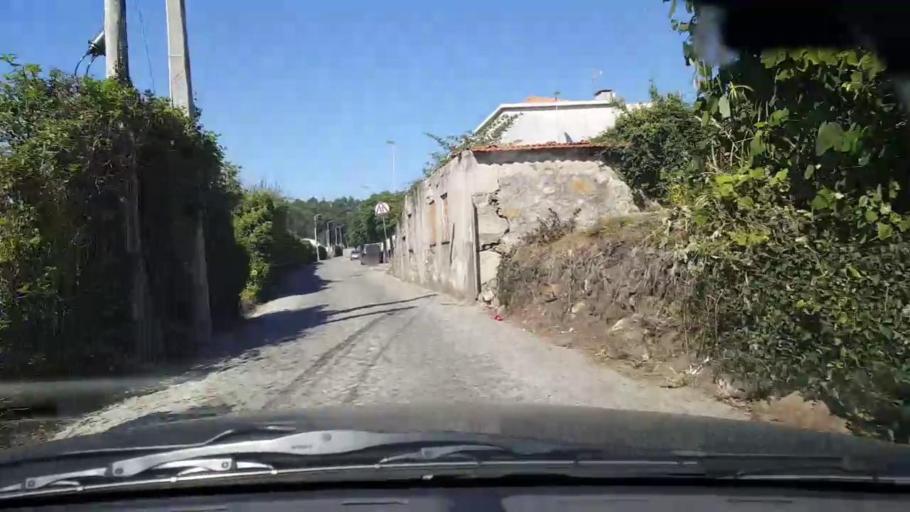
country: PT
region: Porto
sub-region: Matosinhos
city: Lavra
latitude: 41.2983
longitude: -8.7249
